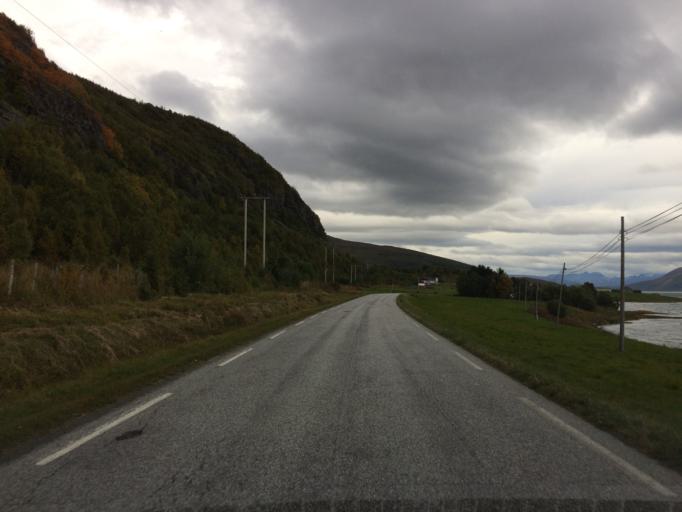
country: NO
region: Troms
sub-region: Sorreisa
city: Sorreisa
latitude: 69.5240
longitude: 18.2426
